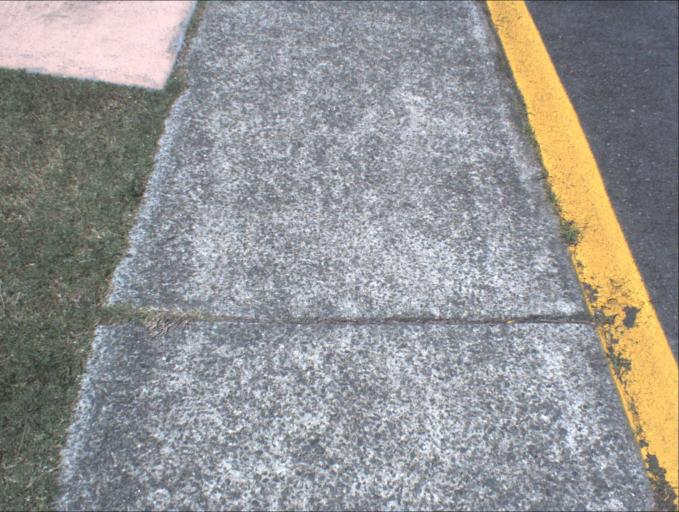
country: AU
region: Queensland
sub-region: Logan
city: Rochedale South
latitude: -27.6032
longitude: 153.1102
